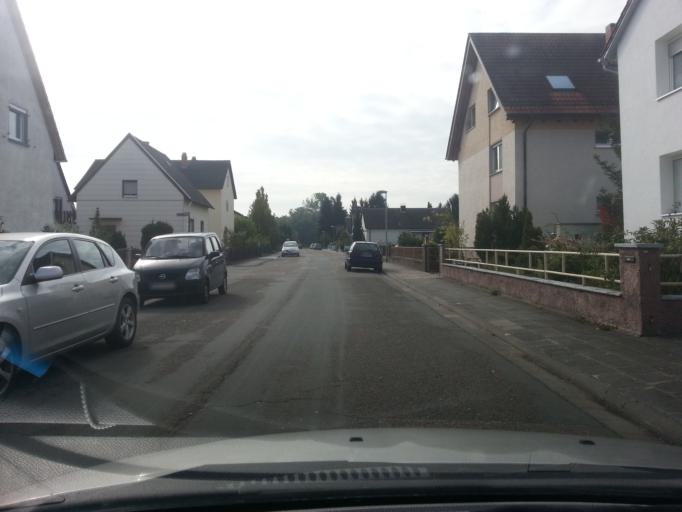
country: DE
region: Rheinland-Pfalz
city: Hassloch
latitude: 49.3498
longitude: 8.2550
